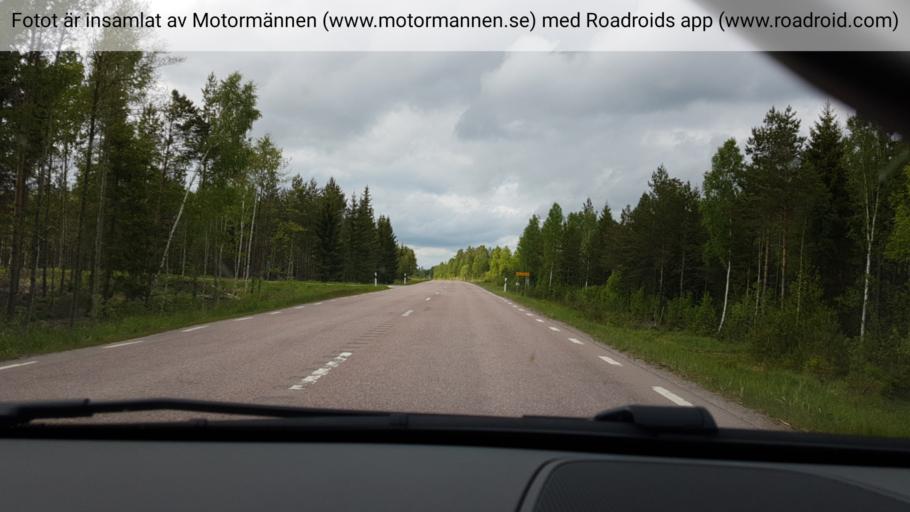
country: SE
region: Uppsala
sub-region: Tierps Kommun
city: Tierp
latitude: 60.2929
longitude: 17.5800
